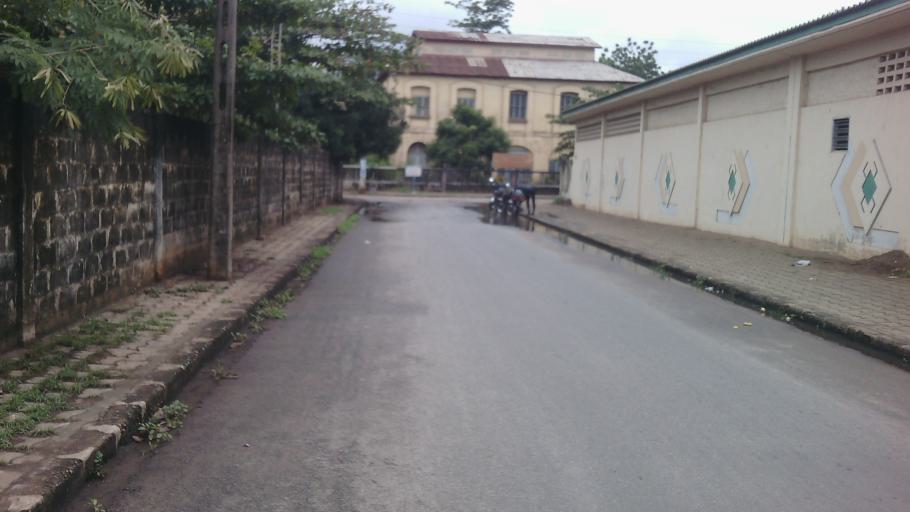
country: BJ
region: Queme
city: Porto-Novo
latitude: 6.4732
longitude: 2.6142
